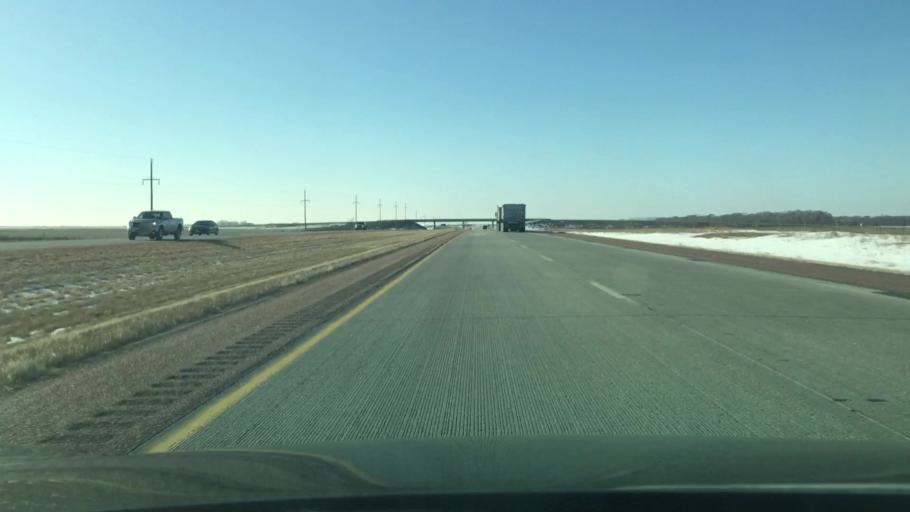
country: US
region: South Dakota
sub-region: Davison County
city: Mitchell
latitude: 43.6960
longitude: -98.1794
